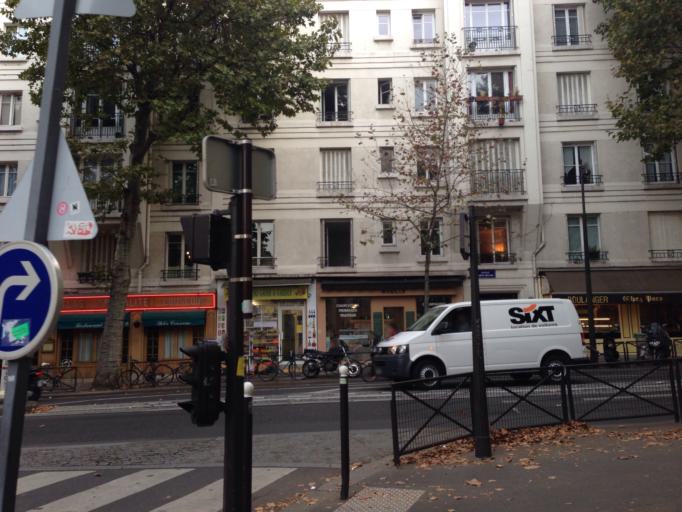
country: FR
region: Ile-de-France
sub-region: Departement de Seine-Saint-Denis
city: Le Pre-Saint-Gervais
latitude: 48.8762
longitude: 2.3768
